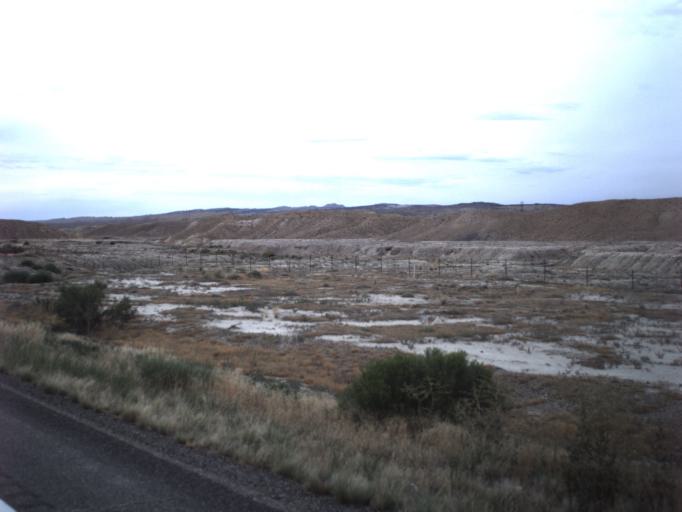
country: US
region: Utah
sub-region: Carbon County
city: East Carbon City
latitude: 39.2876
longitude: -110.3516
